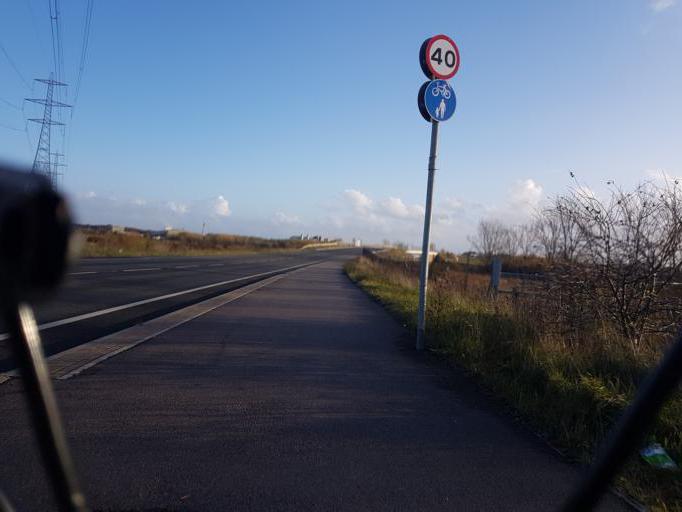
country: GB
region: England
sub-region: Kent
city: Sittingbourne
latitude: 51.3585
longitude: 0.7517
